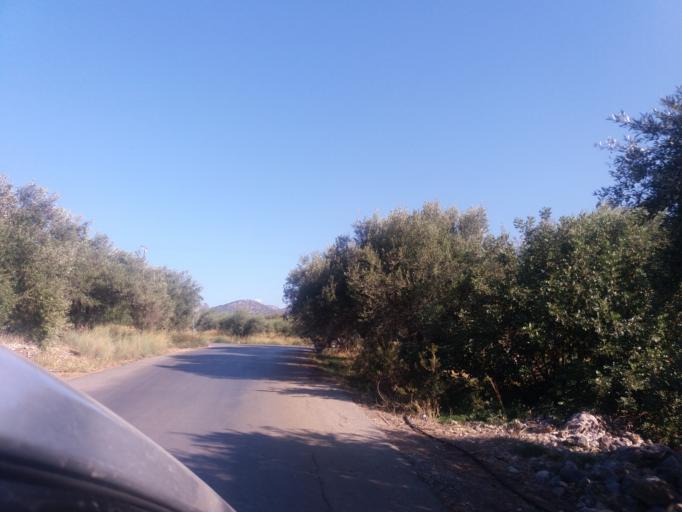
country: GR
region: Crete
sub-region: Nomos Irakleiou
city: Malia
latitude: 35.2903
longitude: 25.4902
